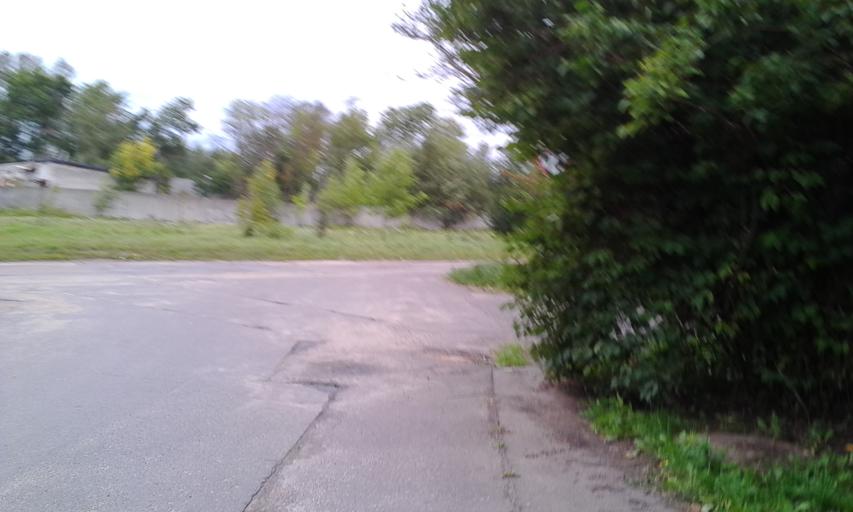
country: BY
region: Minsk
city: Minsk
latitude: 53.9472
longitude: 27.5890
